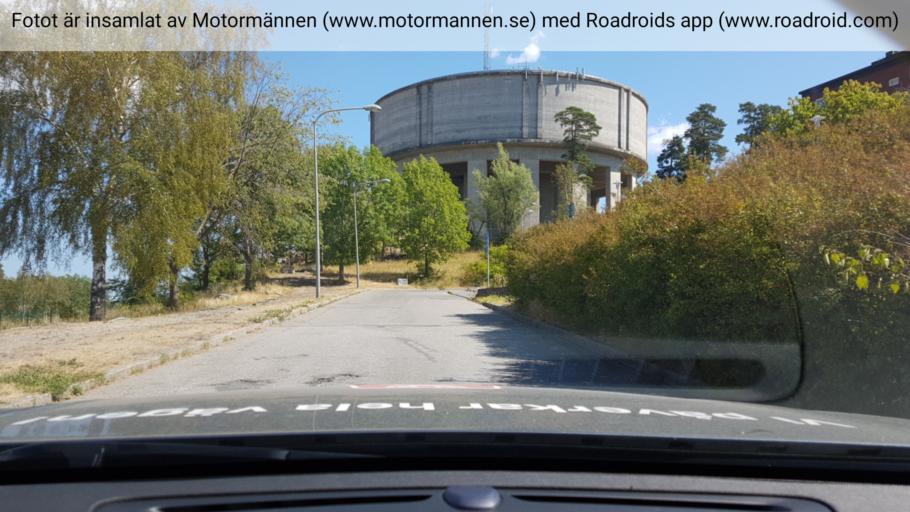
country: SE
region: Stockholm
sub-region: Stockholms Kommun
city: Kista
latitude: 59.3990
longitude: 17.8952
